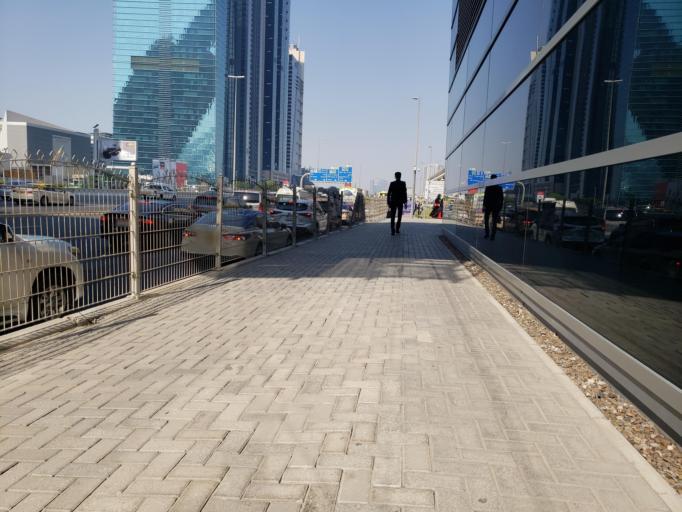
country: AE
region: Ash Shariqah
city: Sharjah
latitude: 25.2252
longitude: 55.2851
